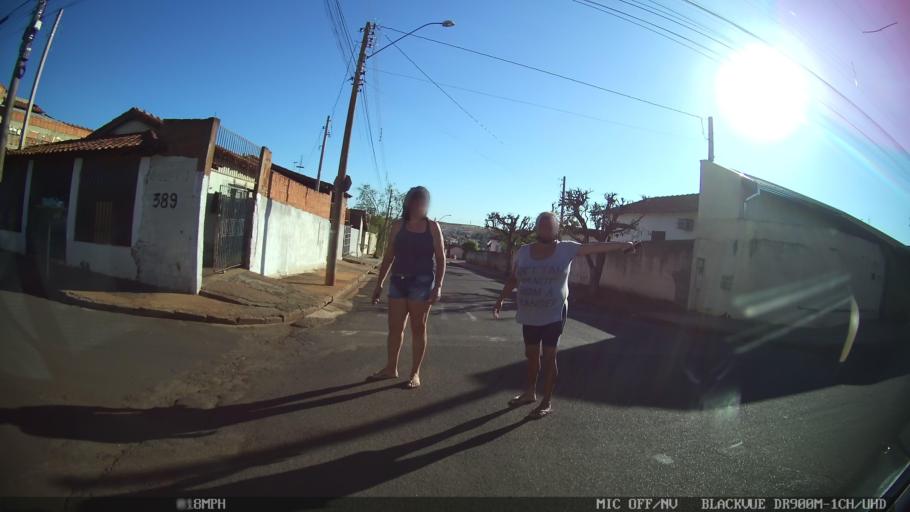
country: BR
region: Sao Paulo
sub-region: Olimpia
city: Olimpia
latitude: -20.7297
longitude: -48.9089
